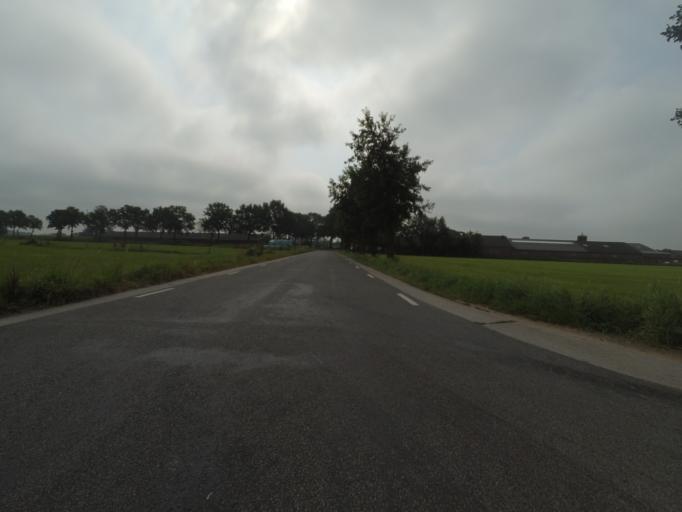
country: NL
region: Gelderland
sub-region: Gemeente Barneveld
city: Kootwijkerbroek
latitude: 52.1444
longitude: 5.6730
